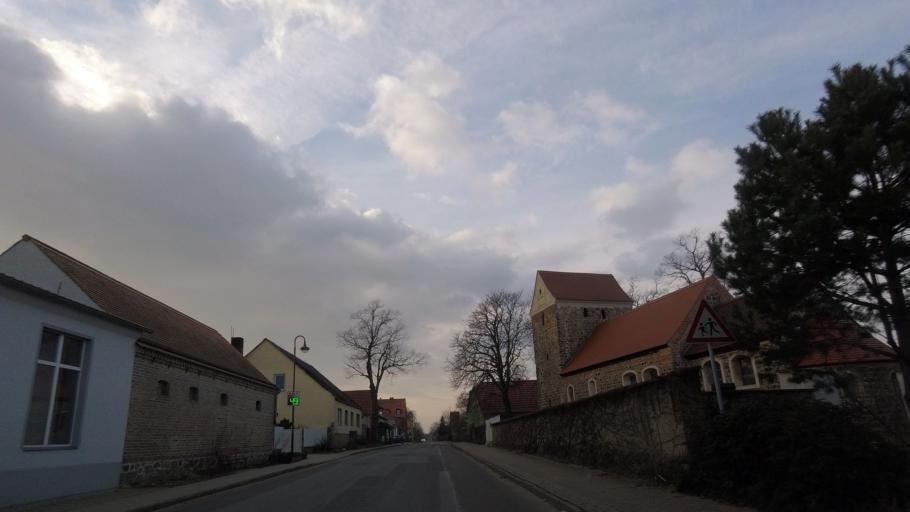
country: DE
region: Brandenburg
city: Belzig
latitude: 52.1562
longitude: 12.5300
